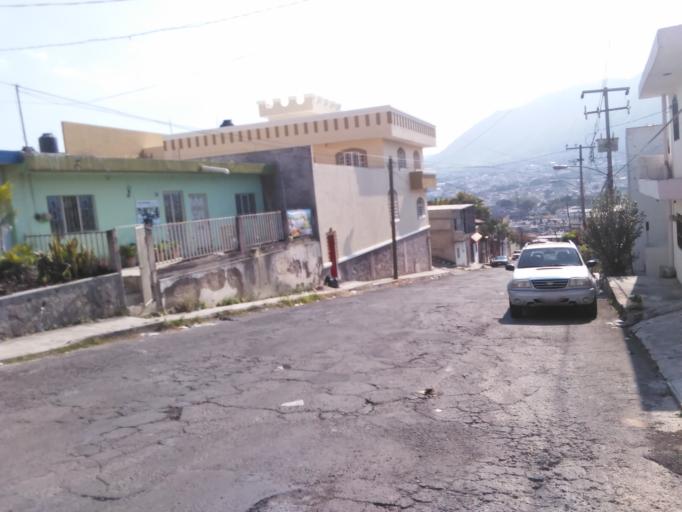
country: MX
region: Nayarit
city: Tepic
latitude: 21.5218
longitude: -104.9125
